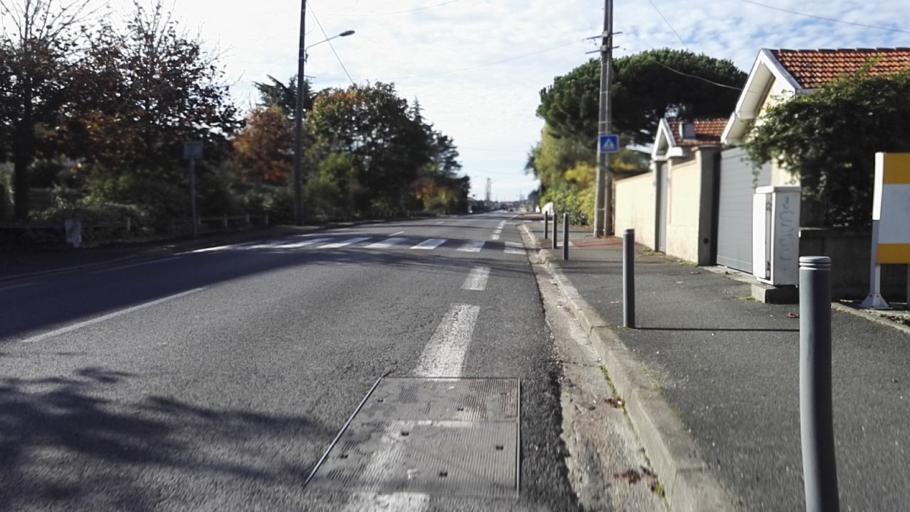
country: FR
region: Aquitaine
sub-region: Departement de la Gironde
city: Merignac
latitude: 44.8563
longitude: -0.6399
